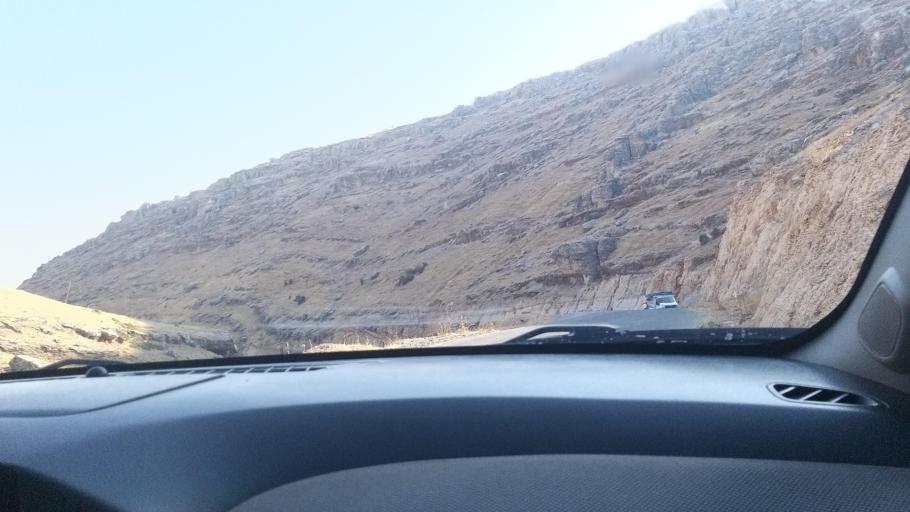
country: TR
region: Diyarbakir
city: Silvan
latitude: 38.1656
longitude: 41.0020
